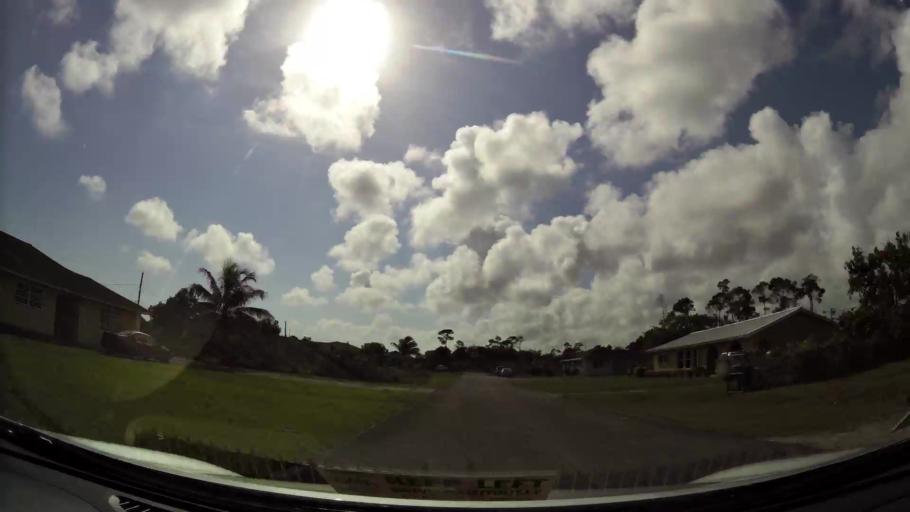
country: BS
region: Freeport
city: Lucaya
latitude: 26.5301
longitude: -78.6794
